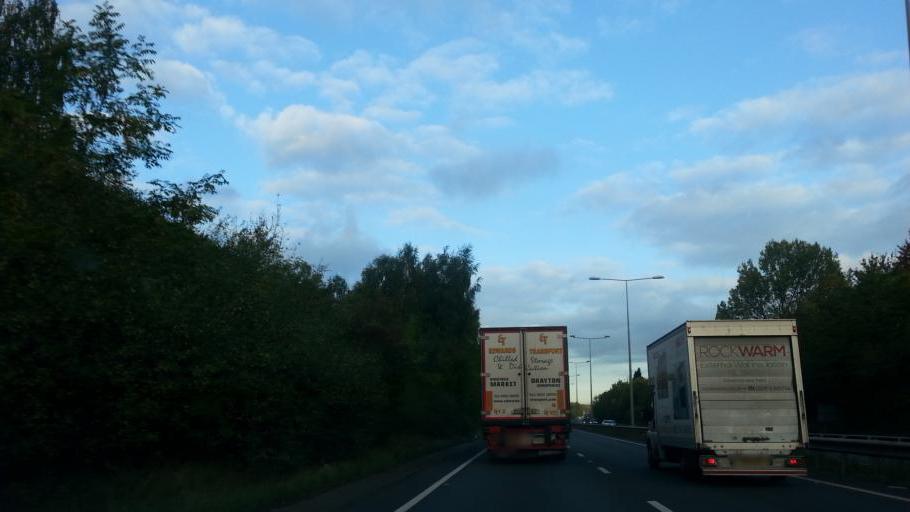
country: GB
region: England
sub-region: Staffordshire
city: Fazeley
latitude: 52.6078
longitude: -1.6531
